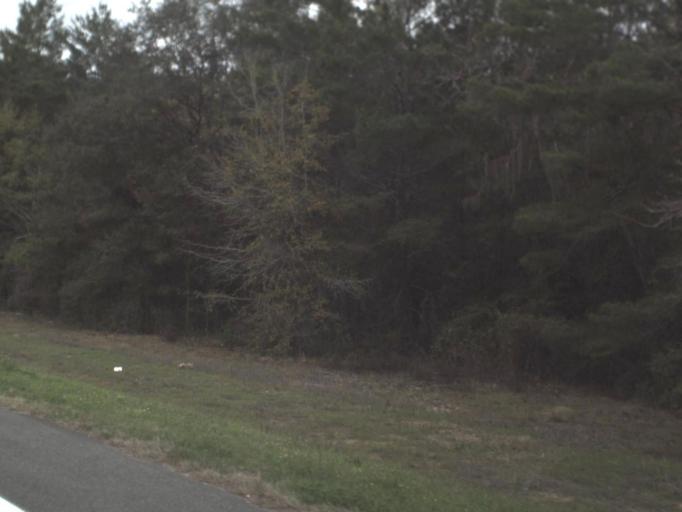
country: US
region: Florida
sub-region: Gadsden County
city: Quincy
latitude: 30.4701
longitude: -84.6352
